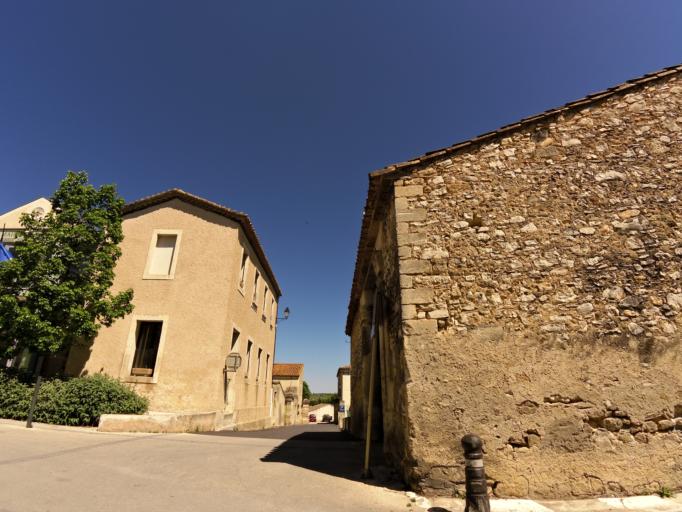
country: FR
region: Languedoc-Roussillon
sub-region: Departement de l'Herault
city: Assas
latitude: 43.7017
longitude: 3.9001
